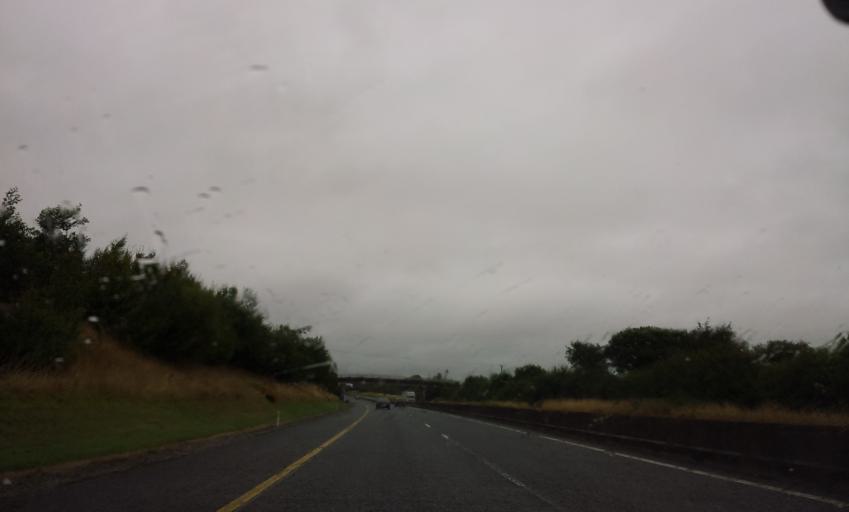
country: IE
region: Munster
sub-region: County Cork
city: Rathcormac
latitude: 52.0791
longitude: -8.2988
